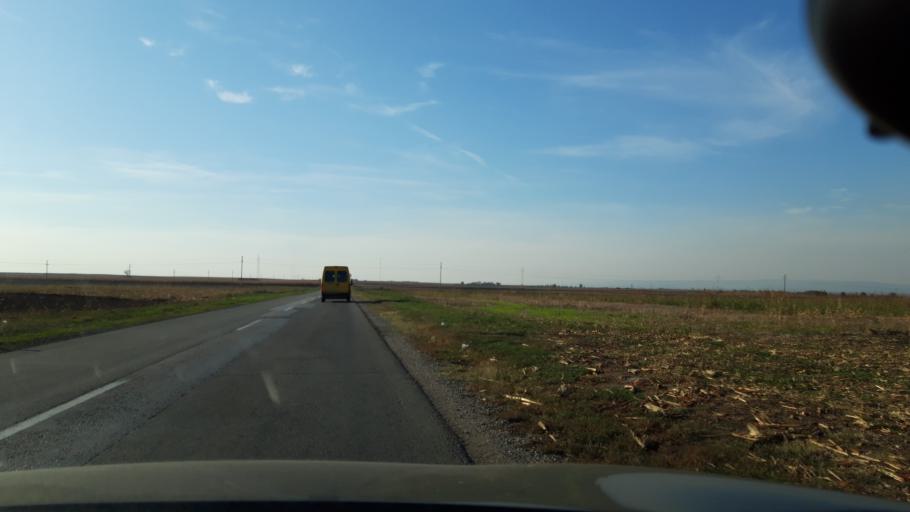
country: RS
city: Putinci
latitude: 45.0066
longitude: 19.9053
